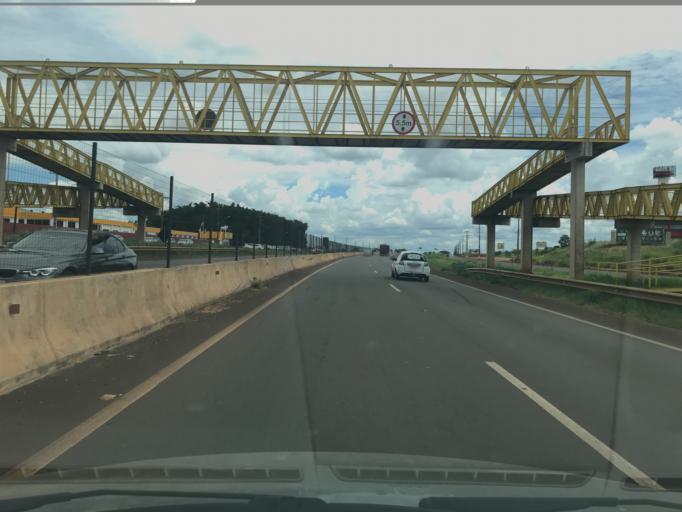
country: BR
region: Parana
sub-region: Paicandu
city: Paicandu
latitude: -23.4537
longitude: -52.0113
